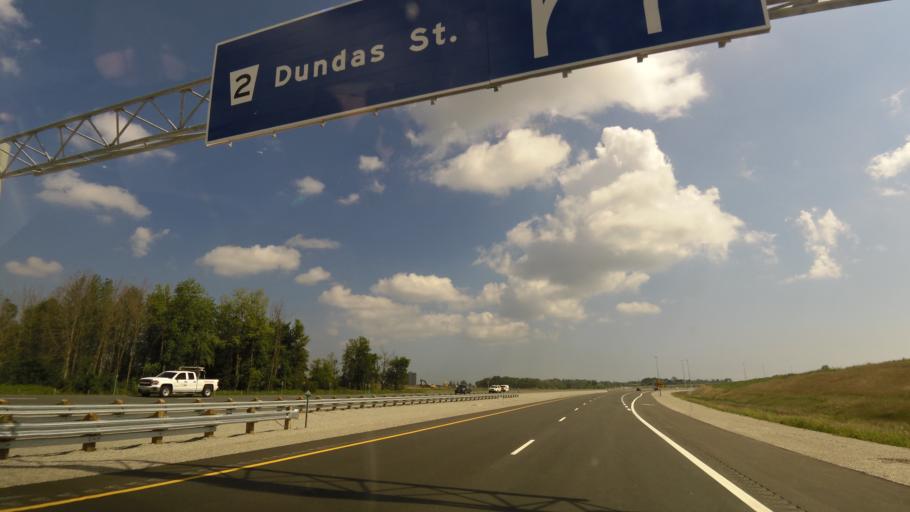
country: CA
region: Ontario
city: Ajax
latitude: 43.8798
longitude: -78.9819
